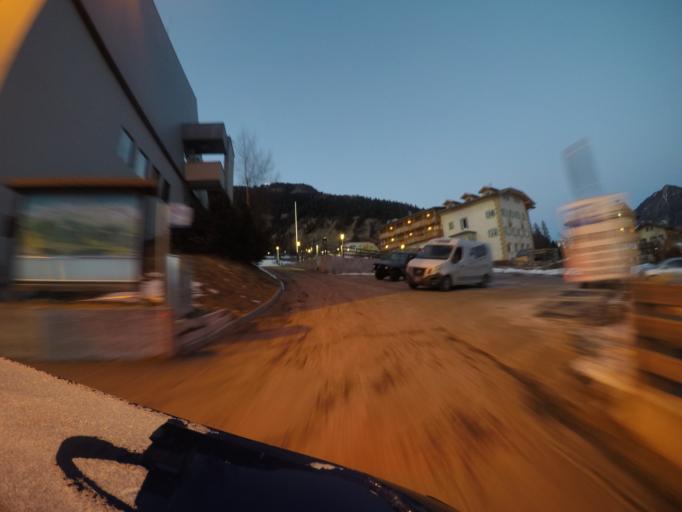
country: IT
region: Trentino-Alto Adige
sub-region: Provincia di Trento
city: Vigo di Fassa
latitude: 46.4211
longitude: 11.6715
